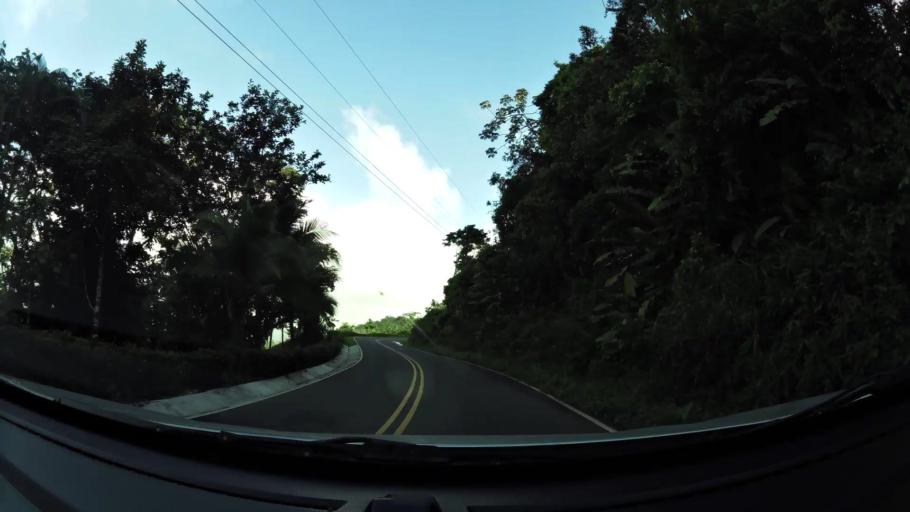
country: CR
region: Limon
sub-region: Canton de Siquirres
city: Siquirres
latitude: 10.0495
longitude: -83.5494
